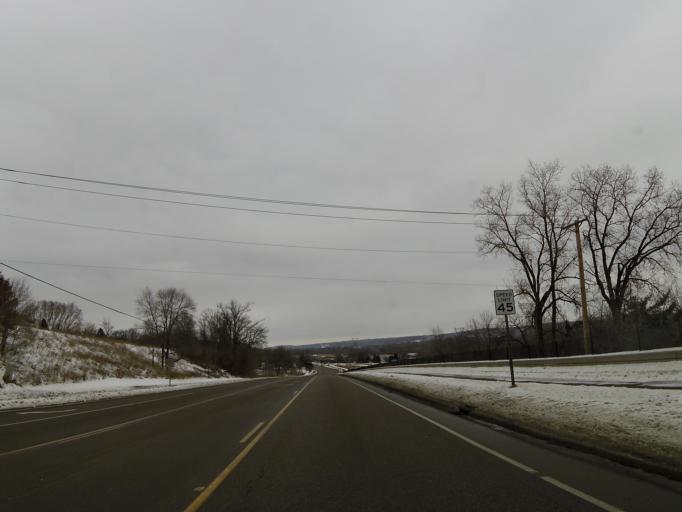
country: US
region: Minnesota
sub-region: Dakota County
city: Inver Grove Heights
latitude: 44.8483
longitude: -93.0203
